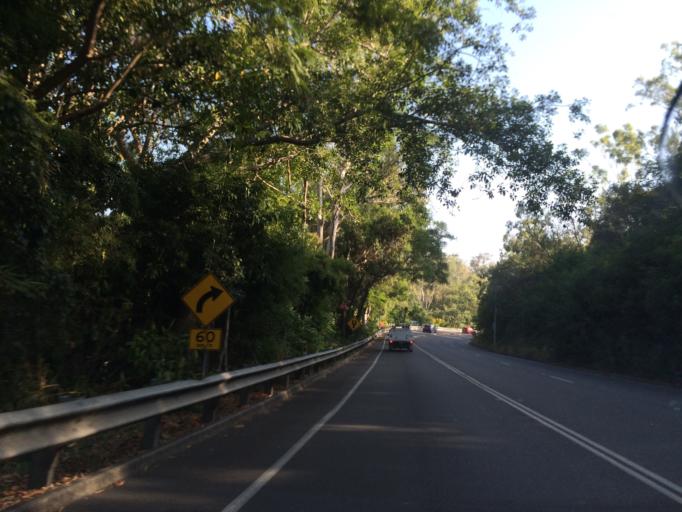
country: AU
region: Queensland
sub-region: Brisbane
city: Kenmore Hills
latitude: -27.5132
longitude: 152.9333
